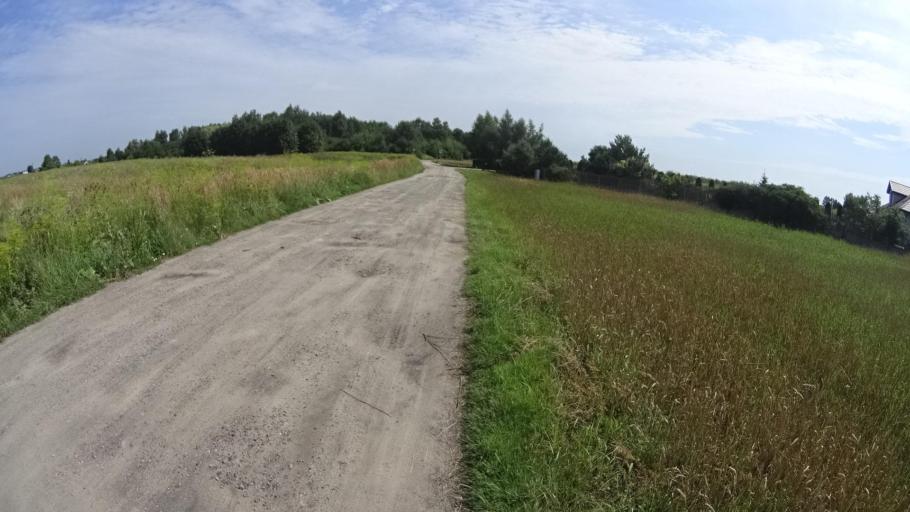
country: PL
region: Masovian Voivodeship
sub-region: Powiat warszawski zachodni
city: Ozarow Mazowiecki
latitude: 52.1926
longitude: 20.7833
